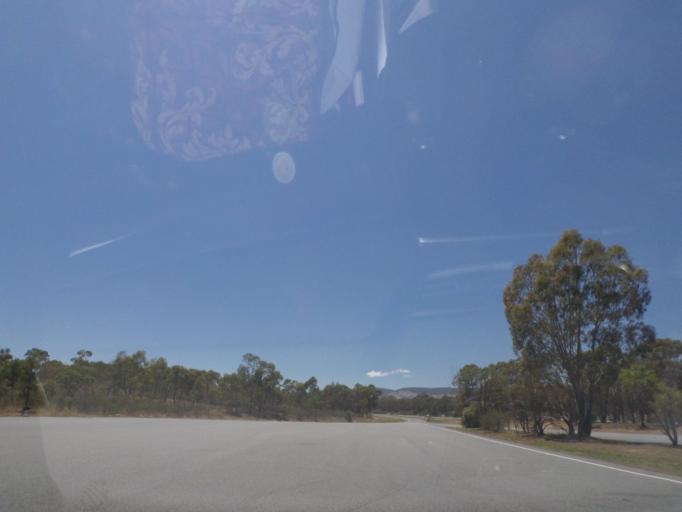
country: AU
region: Victoria
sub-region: Benalla
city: Benalla
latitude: -36.7137
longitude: 145.6352
